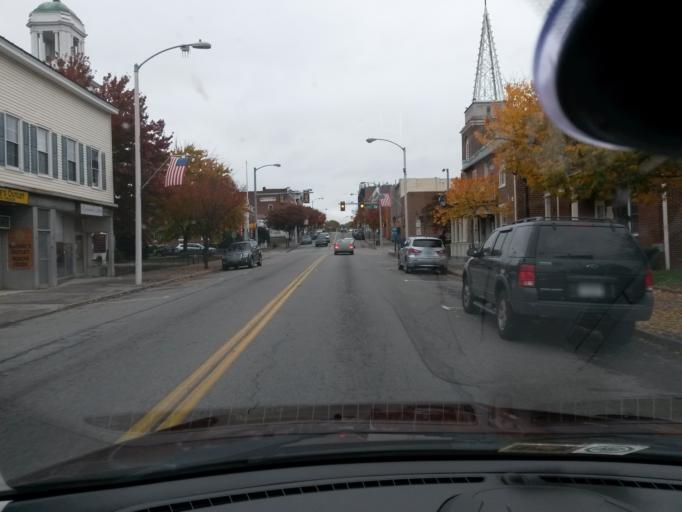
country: US
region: Virginia
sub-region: City of Salem
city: Salem
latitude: 37.2928
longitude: -80.0574
